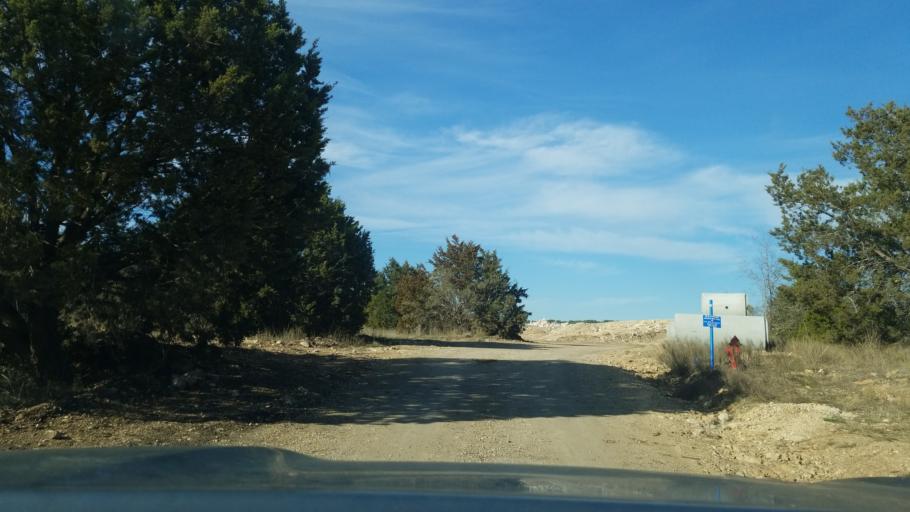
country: US
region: Texas
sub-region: Comal County
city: Canyon Lake
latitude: 29.7815
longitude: -98.2880
